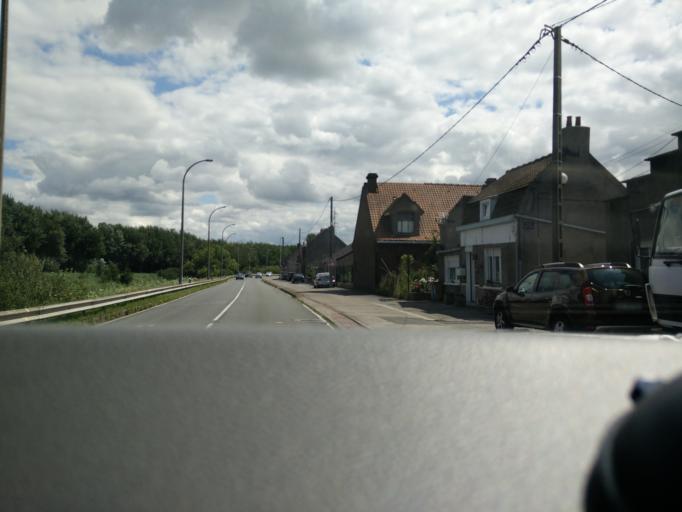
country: FR
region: Nord-Pas-de-Calais
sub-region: Departement du Nord
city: Coudekerque-Branche
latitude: 50.9986
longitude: 2.3895
